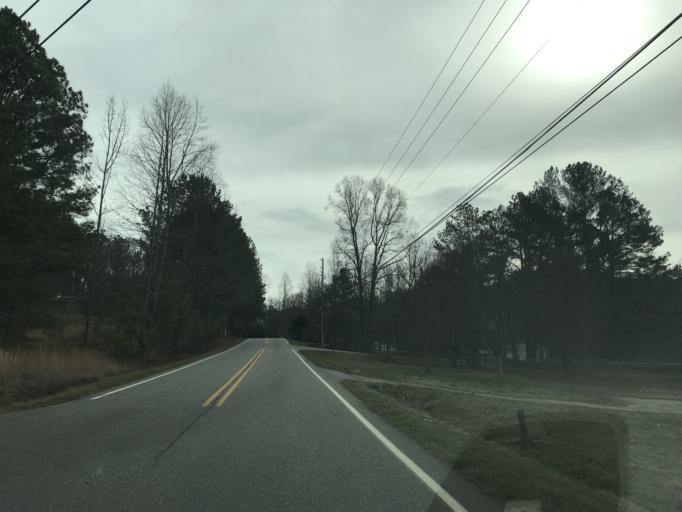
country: US
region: Georgia
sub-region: Cherokee County
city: Canton
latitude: 34.2016
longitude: -84.3869
